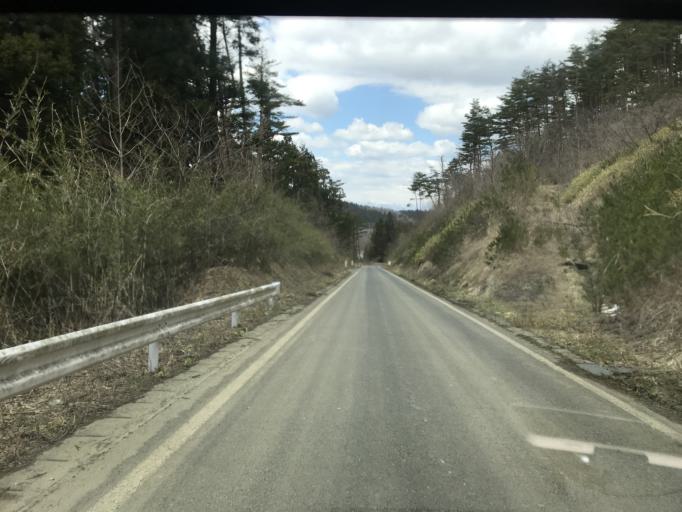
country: JP
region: Iwate
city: Ichinoseki
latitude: 38.9508
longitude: 141.0906
